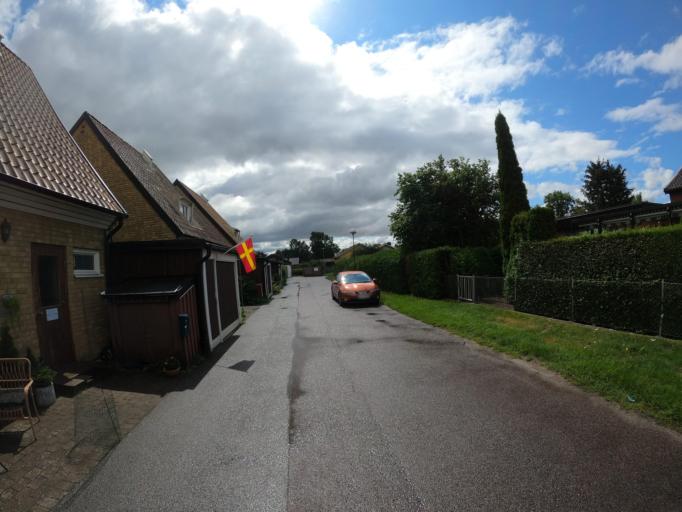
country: SE
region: Skane
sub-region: Hoors Kommun
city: Loberod
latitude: 55.7259
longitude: 13.4598
